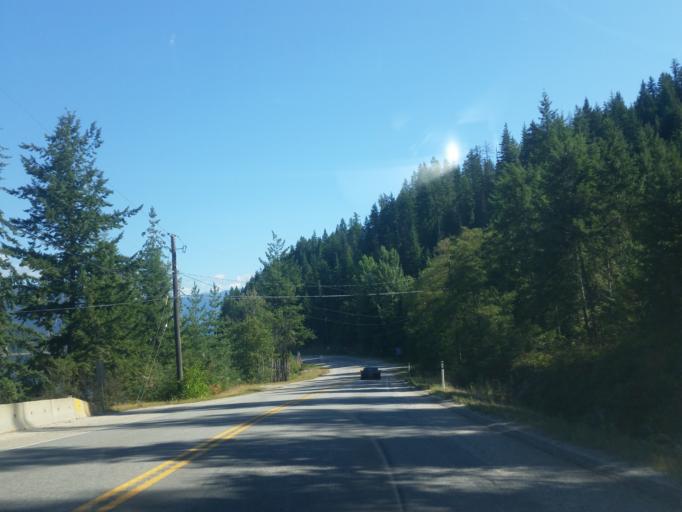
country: CA
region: British Columbia
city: Sicamous
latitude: 50.7719
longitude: -119.0066
